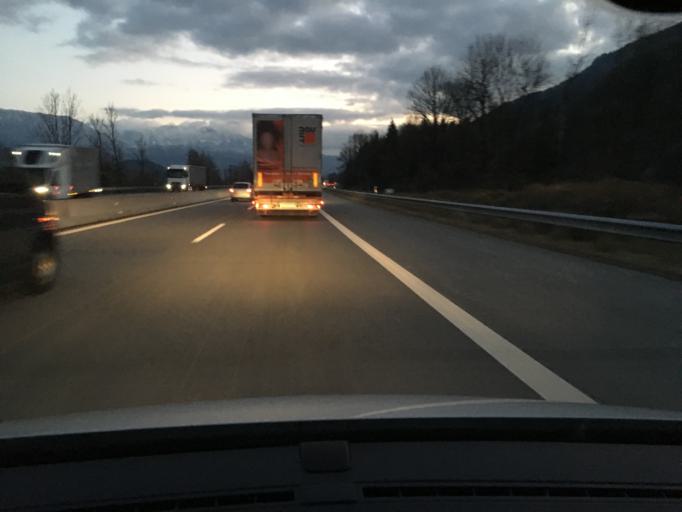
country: AT
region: Tyrol
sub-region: Politischer Bezirk Kufstein
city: Erl
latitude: 47.6982
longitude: 12.1614
